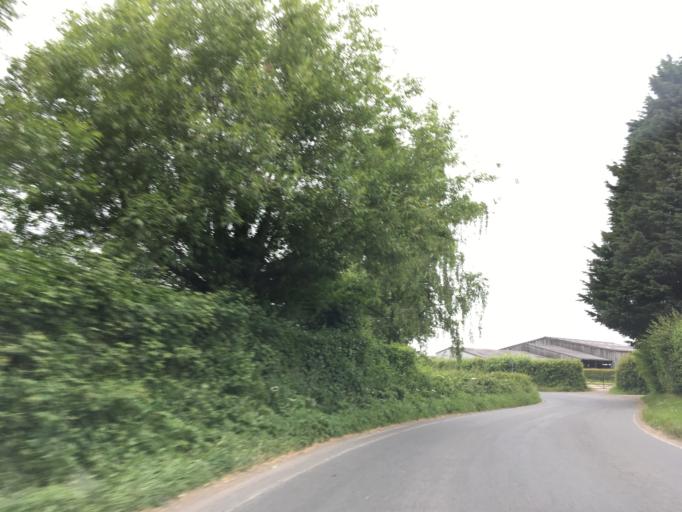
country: GB
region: England
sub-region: Gloucestershire
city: Stonehouse
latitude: 51.7797
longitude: -2.3663
